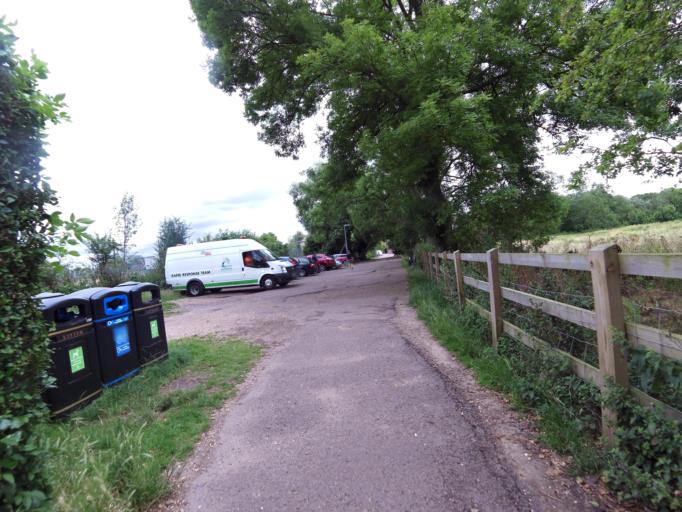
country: GB
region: England
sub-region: Cambridgeshire
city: Cambridge
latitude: 52.1922
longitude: 0.1051
